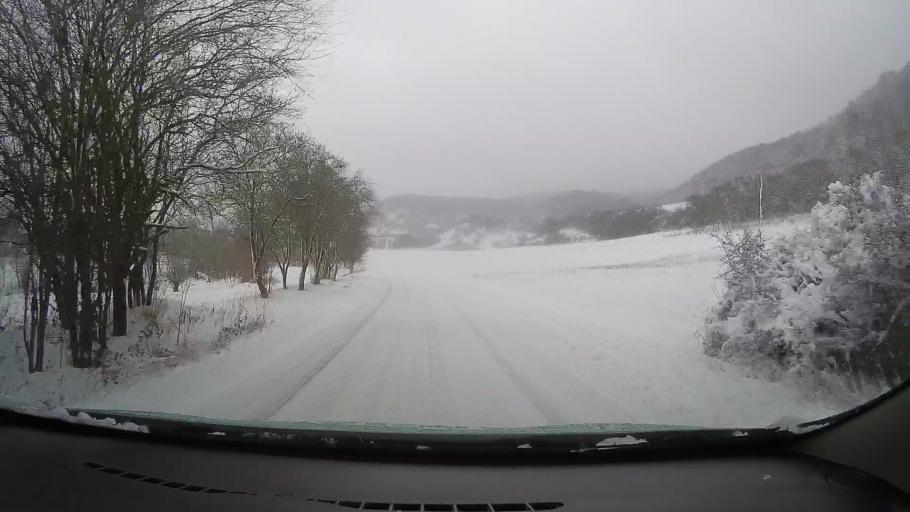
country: RO
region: Hunedoara
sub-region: Comuna Carjiti
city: Carjiti
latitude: 45.8418
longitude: 22.8352
